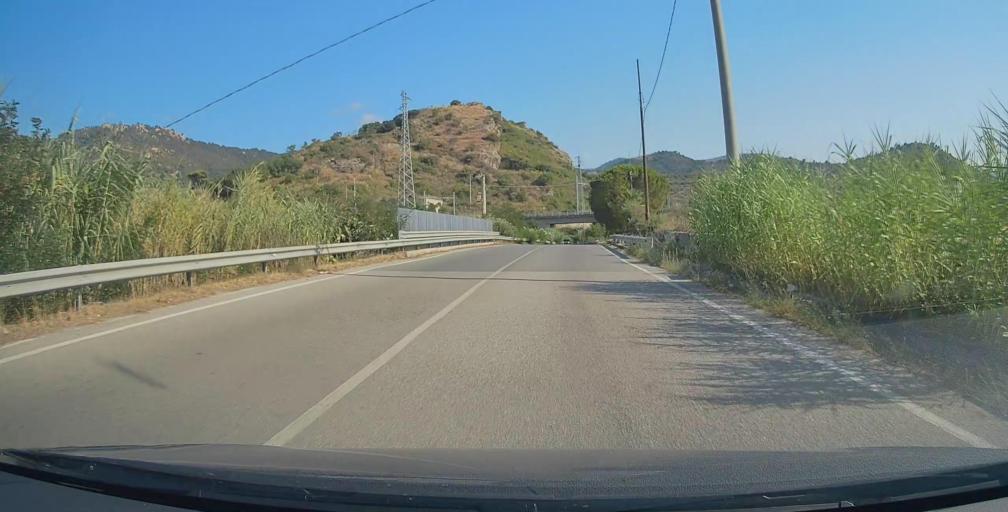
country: IT
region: Sicily
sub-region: Messina
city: Patti
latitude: 38.1413
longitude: 14.9966
